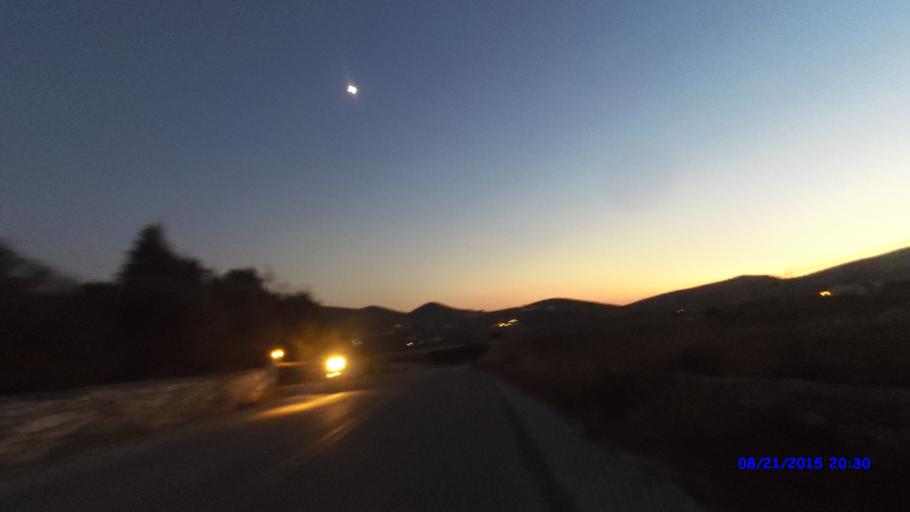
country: GR
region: South Aegean
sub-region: Nomos Kykladon
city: Antiparos
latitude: 36.9787
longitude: 25.0609
